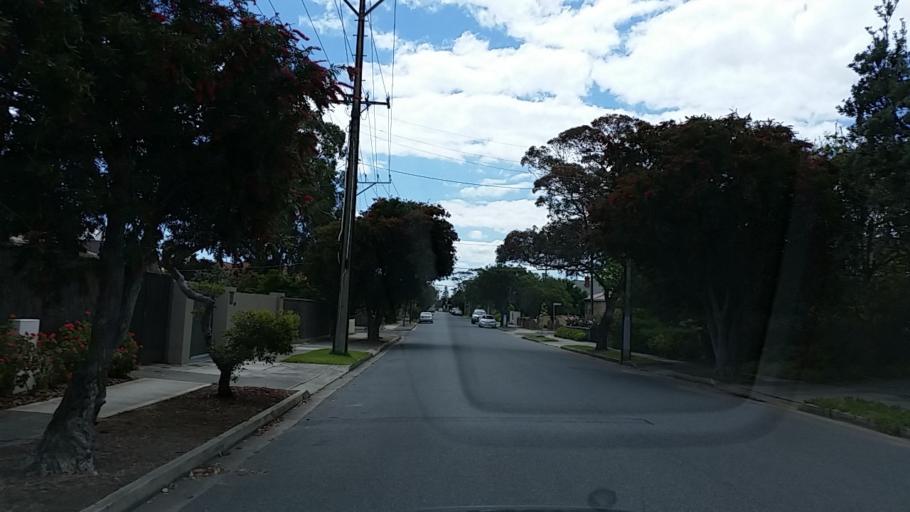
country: AU
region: South Australia
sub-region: Holdfast Bay
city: North Brighton
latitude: -34.9939
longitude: 138.5161
